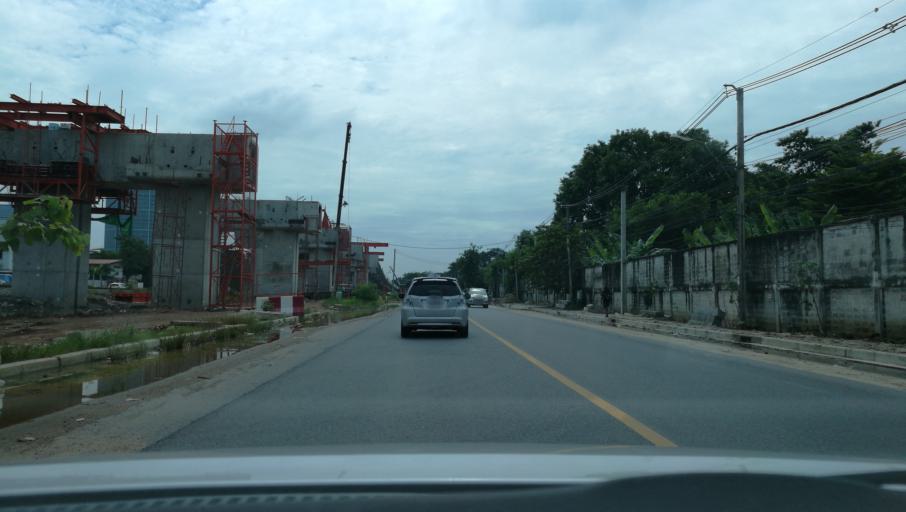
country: TH
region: Bangkok
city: Bang Sue
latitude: 13.7949
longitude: 100.5359
